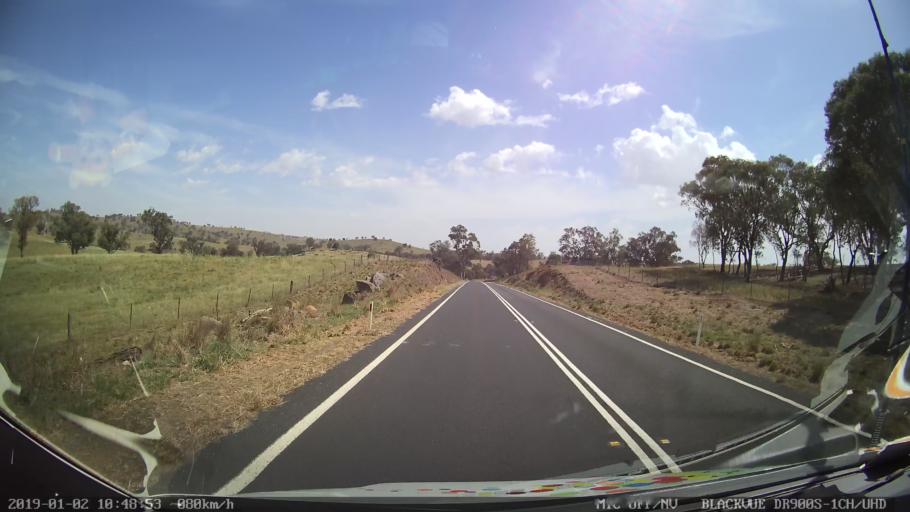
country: AU
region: New South Wales
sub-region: Cootamundra
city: Cootamundra
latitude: -34.7315
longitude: 148.2776
